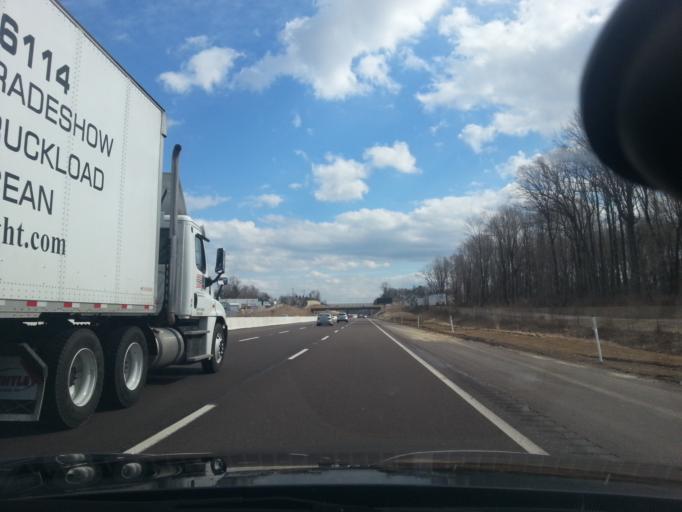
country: US
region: Pennsylvania
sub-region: Montgomery County
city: Blue Bell
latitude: 40.1626
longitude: -75.3009
